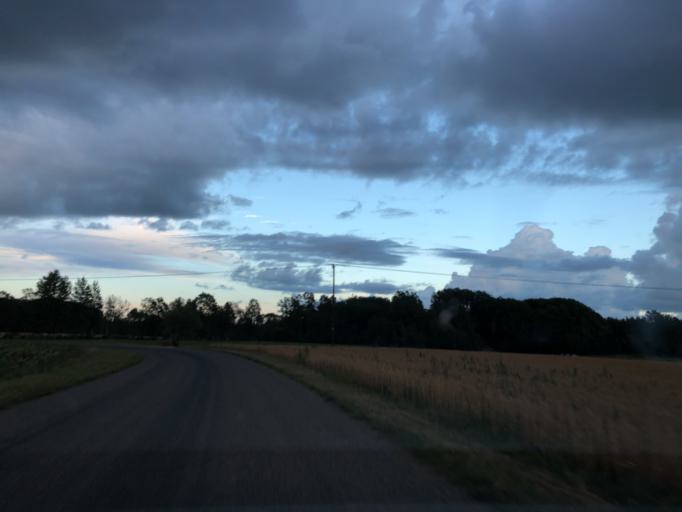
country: EE
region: Laeaene
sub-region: Ridala Parish
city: Uuemoisa
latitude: 58.8882
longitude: 23.6691
